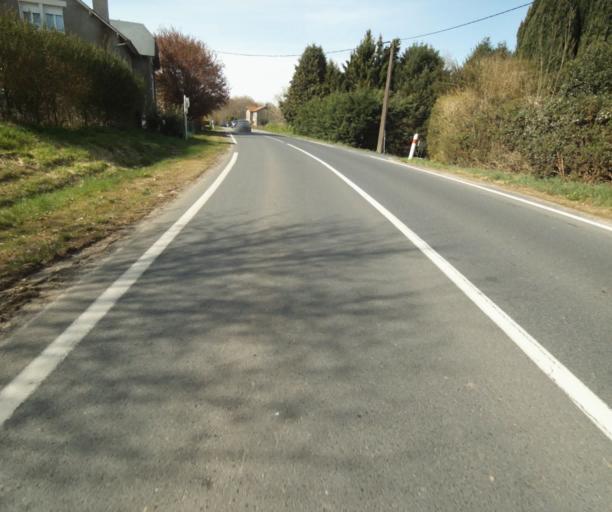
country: FR
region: Limousin
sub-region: Departement de la Correze
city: Seilhac
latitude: 45.3565
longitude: 1.7314
